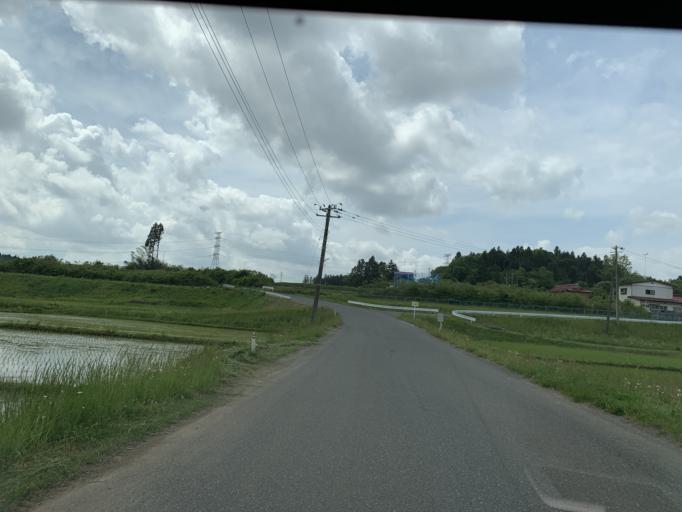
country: JP
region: Iwate
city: Ichinoseki
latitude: 38.8171
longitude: 141.0198
